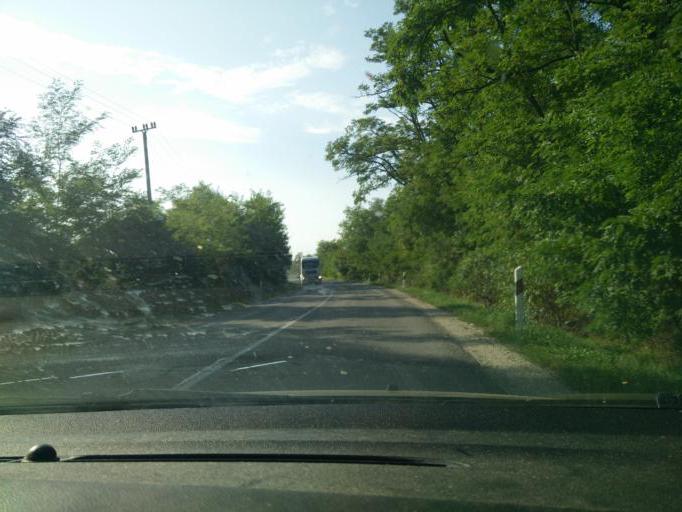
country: HU
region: Pest
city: Piliscsaba
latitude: 47.6505
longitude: 18.8017
